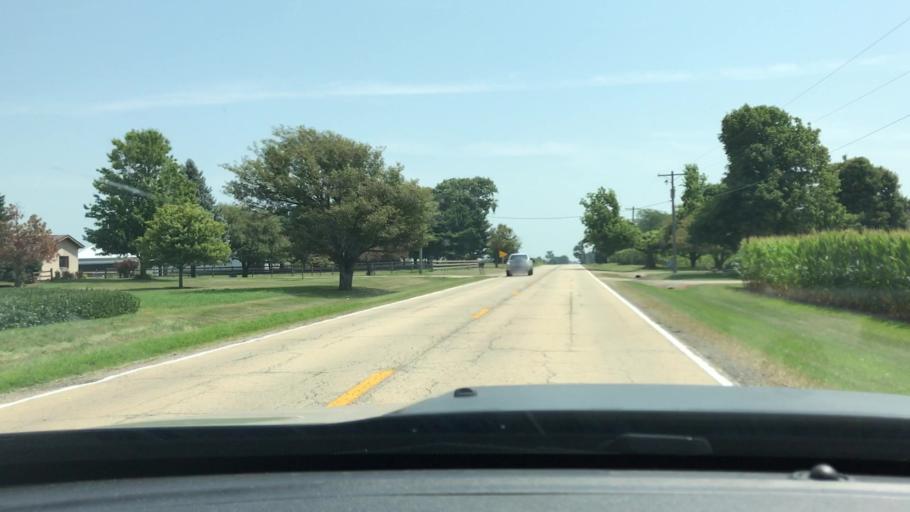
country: US
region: Illinois
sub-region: LaSalle County
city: Earlville
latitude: 41.4689
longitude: -88.9300
